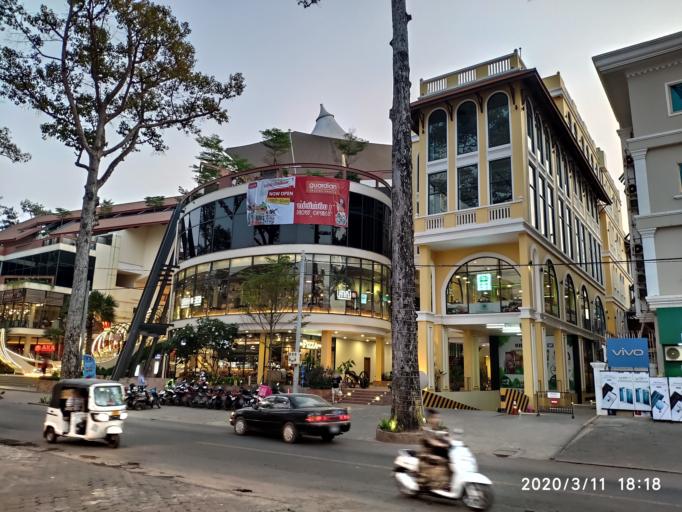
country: KH
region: Siem Reap
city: Siem Reap
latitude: 13.3631
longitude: 103.8570
